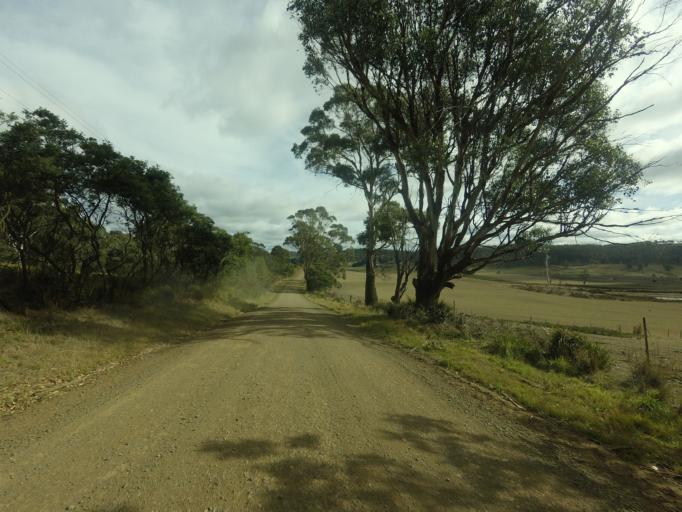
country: AU
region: Tasmania
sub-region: Brighton
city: Bridgewater
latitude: -42.3871
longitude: 147.4056
